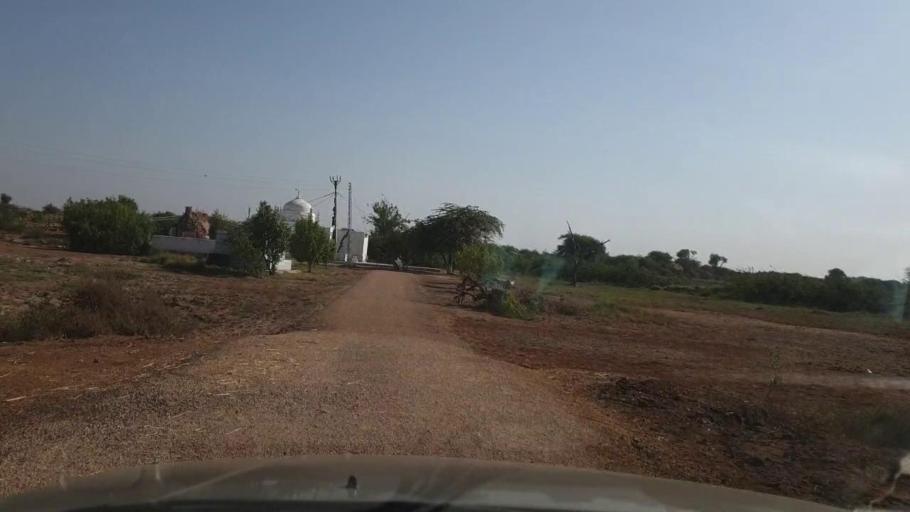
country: PK
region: Sindh
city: Daro Mehar
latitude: 24.9873
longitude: 68.1486
